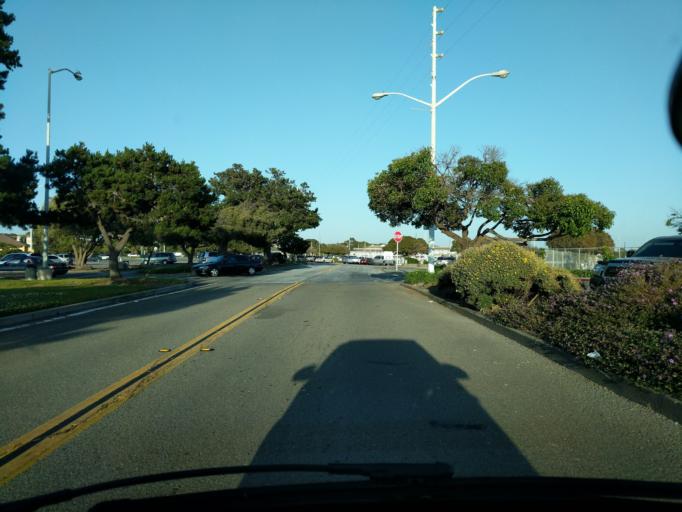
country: US
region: California
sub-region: Alameda County
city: San Leandro
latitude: 37.6986
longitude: -122.1934
